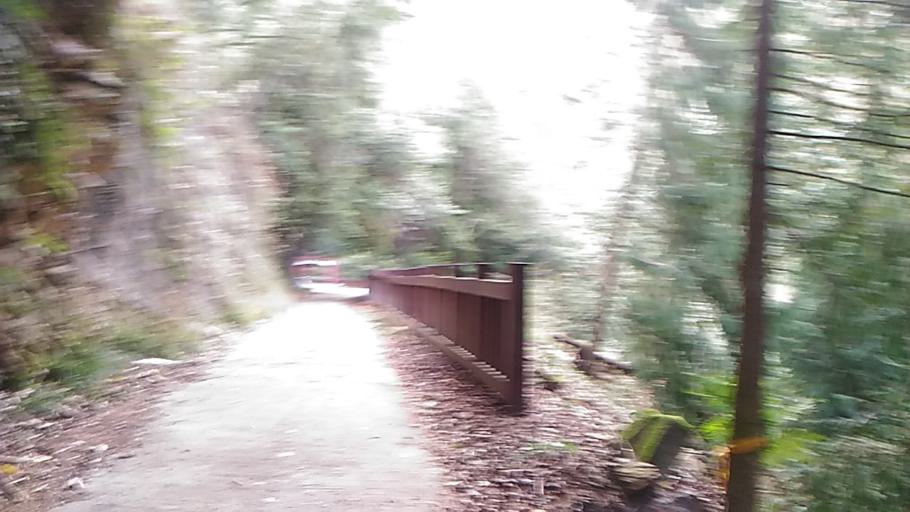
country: TW
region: Taiwan
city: Daxi
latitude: 24.4117
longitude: 121.3028
